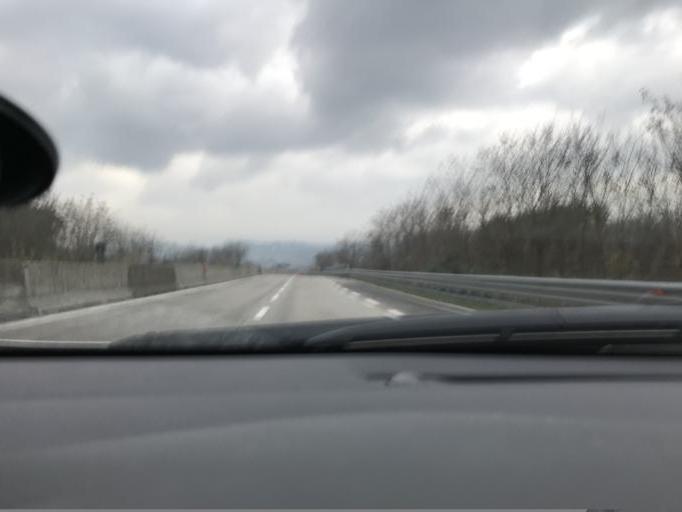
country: IT
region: The Marches
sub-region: Provincia di Ancona
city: Moie
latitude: 43.4949
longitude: 13.1272
